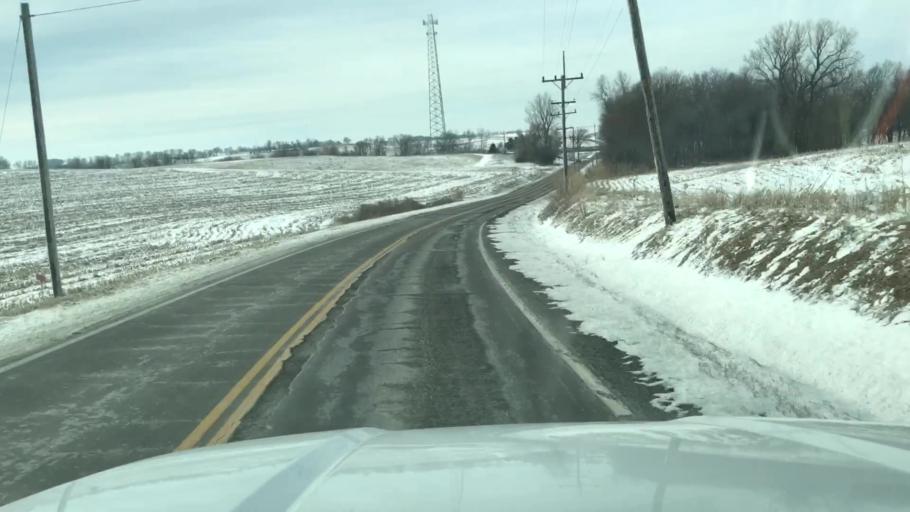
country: US
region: Missouri
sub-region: Holt County
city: Oregon
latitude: 40.0487
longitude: -95.1358
